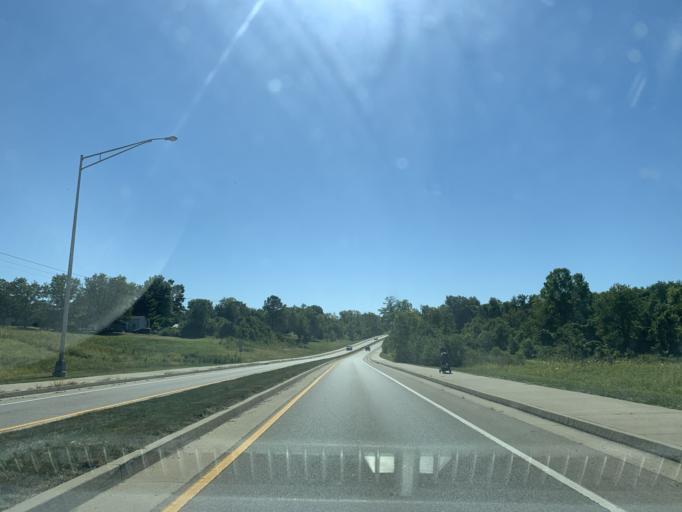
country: US
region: Kentucky
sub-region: Boone County
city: Francisville
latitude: 39.0982
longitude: -84.7179
